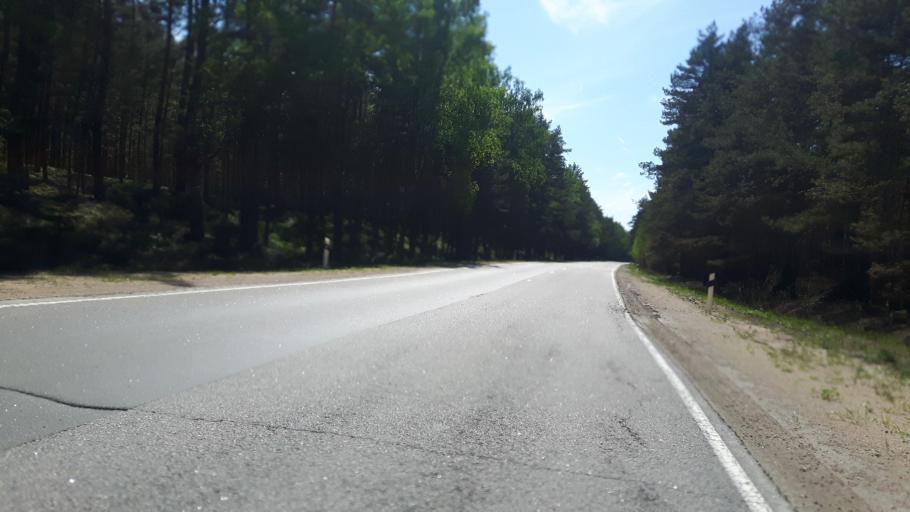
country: RU
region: Leningrad
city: Sista-Palkino
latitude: 59.7754
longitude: 28.8576
